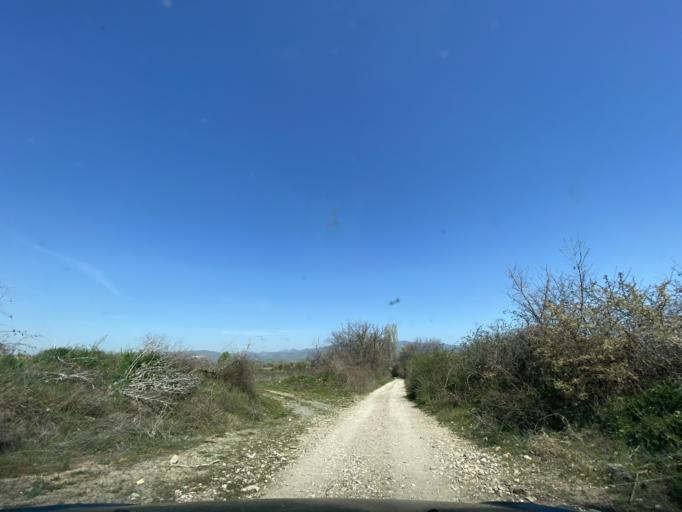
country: MK
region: Zrnovci
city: Zrnovci
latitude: 41.8550
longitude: 22.3892
